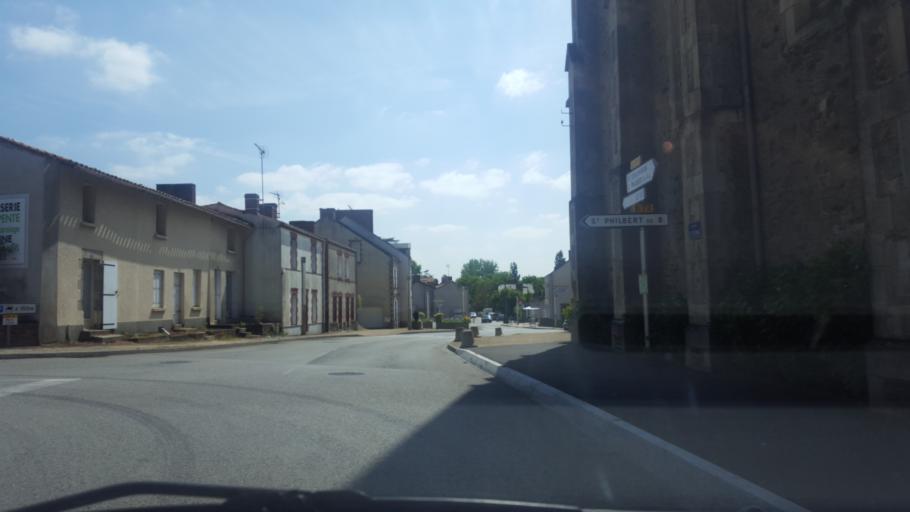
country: FR
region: Pays de la Loire
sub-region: Departement de la Loire-Atlantique
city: La Limouziniere
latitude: 46.9664
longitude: -1.5768
